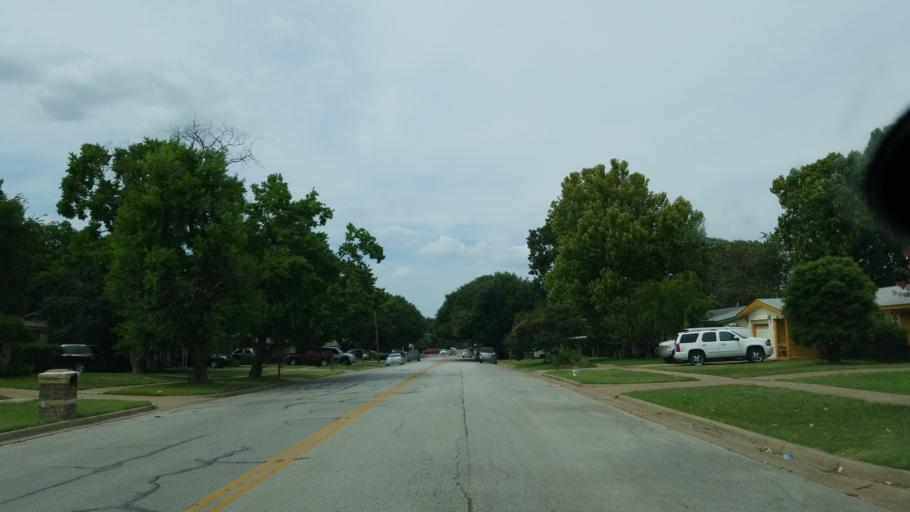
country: US
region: Texas
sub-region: Tarrant County
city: Arlington
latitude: 32.7190
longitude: -97.0834
